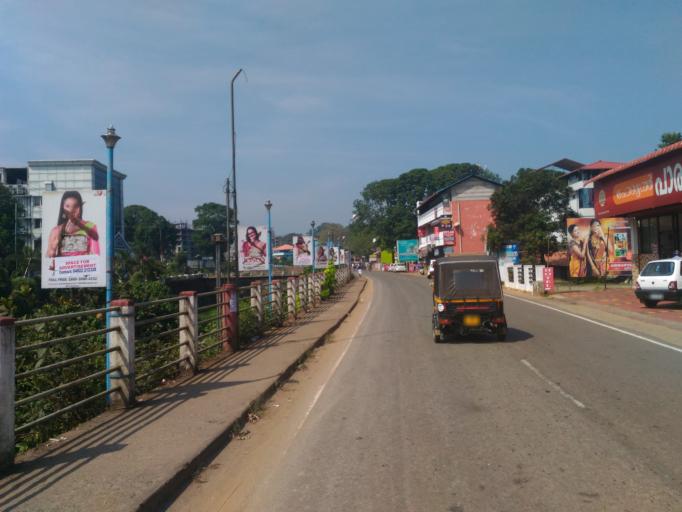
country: IN
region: Kerala
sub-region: Kottayam
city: Lalam
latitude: 9.7124
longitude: 76.6862
